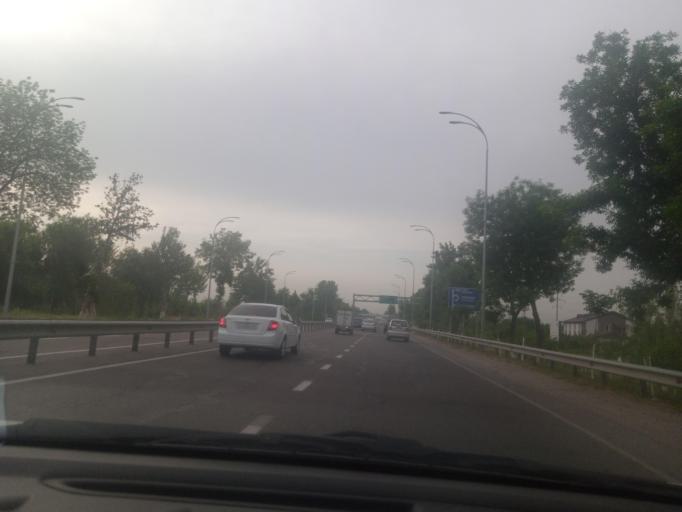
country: UZ
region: Toshkent Shahri
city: Bektemir
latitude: 41.2515
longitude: 69.3873
